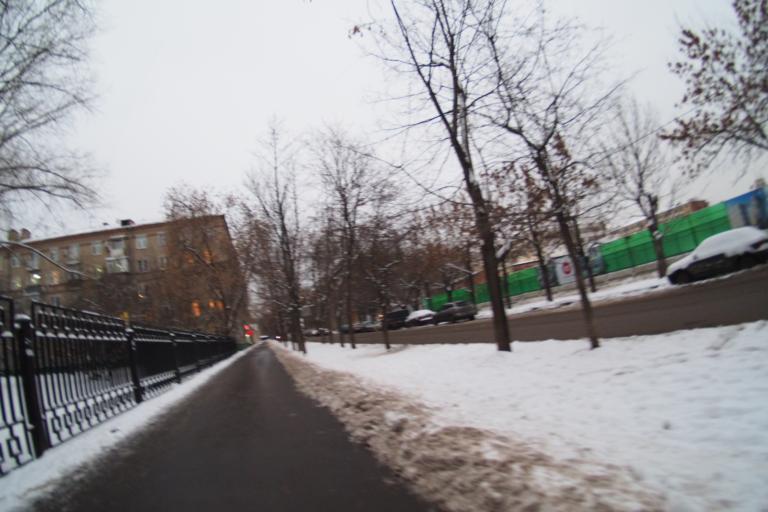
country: RU
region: Moscow
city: Sokol
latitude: 55.7982
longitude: 37.5632
